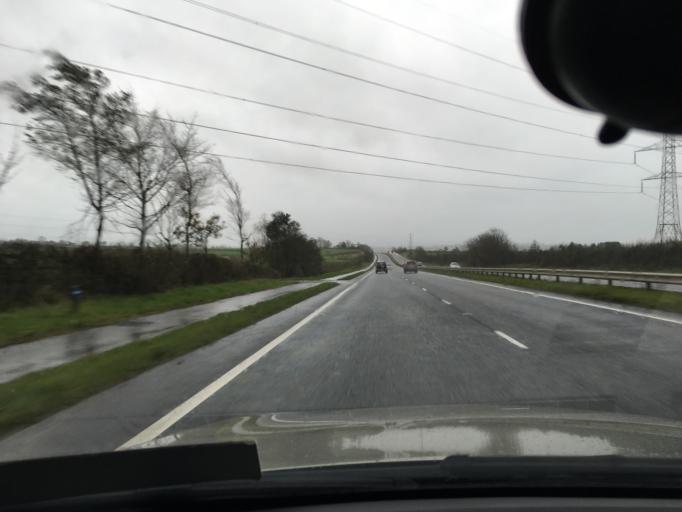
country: GB
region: Northern Ireland
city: Carnmoney
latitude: 54.7202
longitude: -5.9684
